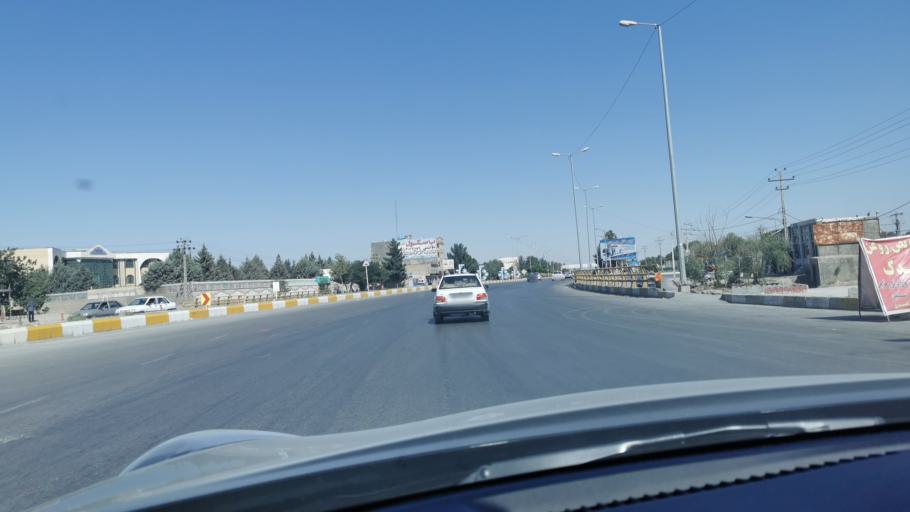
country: IR
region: Razavi Khorasan
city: Chenaran
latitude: 36.6348
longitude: 59.1294
